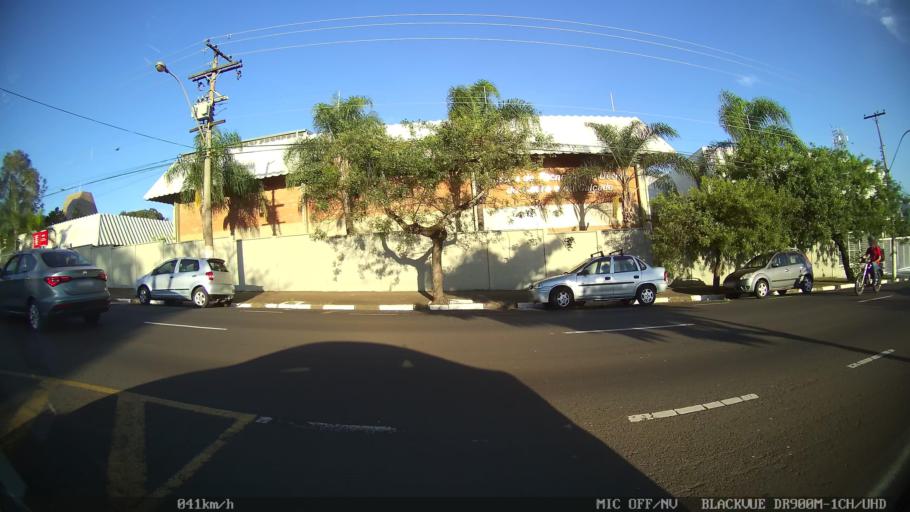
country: BR
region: Sao Paulo
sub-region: Franca
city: Franca
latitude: -20.5176
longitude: -47.3813
